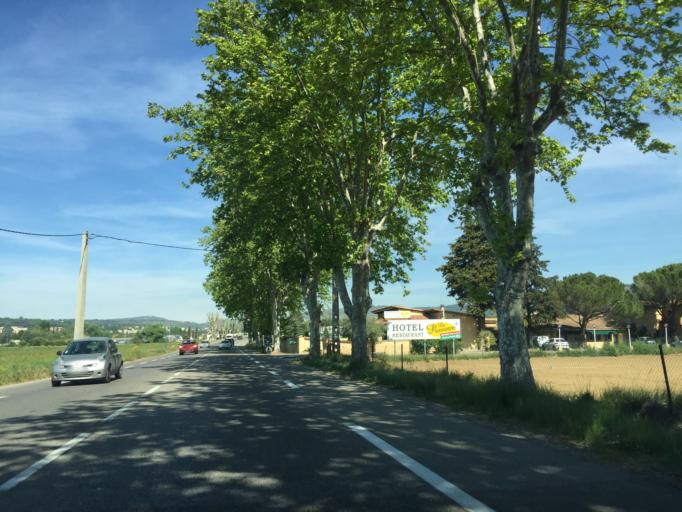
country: FR
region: Provence-Alpes-Cote d'Azur
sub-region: Departement des Alpes-de-Haute-Provence
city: Manosque
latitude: 43.8141
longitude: 5.8032
